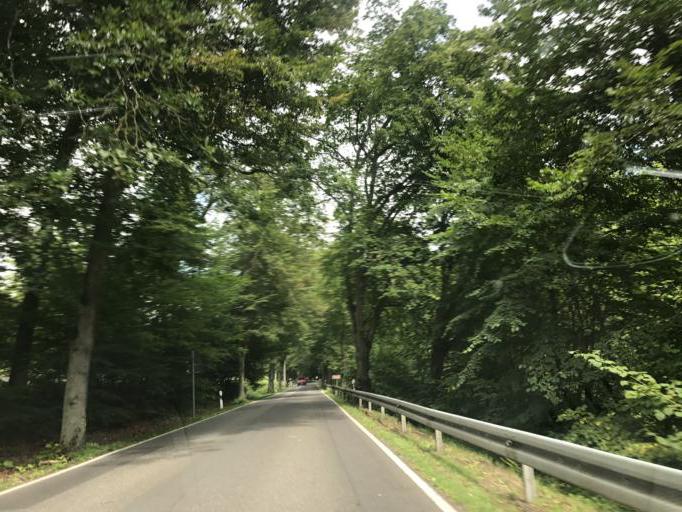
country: DE
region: Brandenburg
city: Rheinsberg
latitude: 53.1808
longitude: 12.8867
